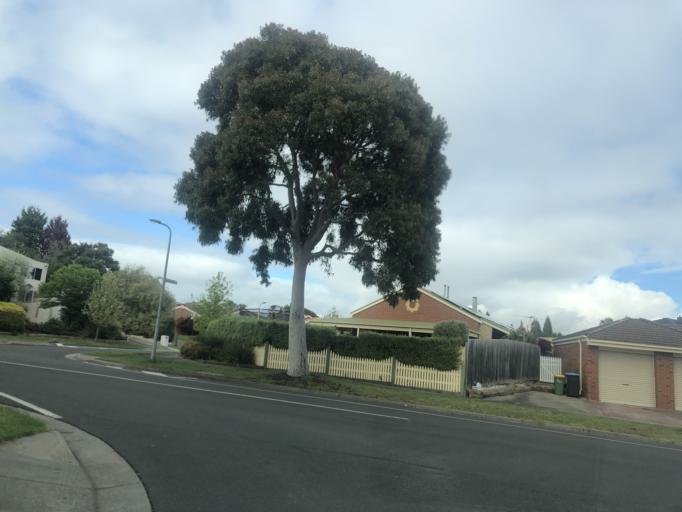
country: AU
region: Victoria
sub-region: Knox
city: Rowville
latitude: -37.9330
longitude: 145.2394
